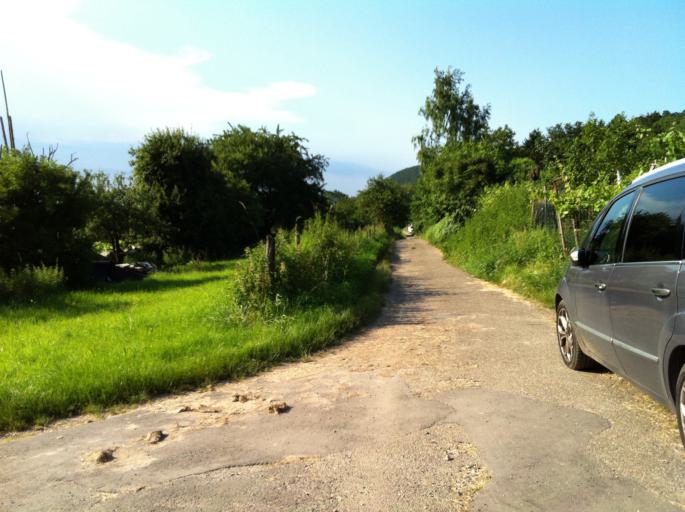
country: DE
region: Baden-Wuerttemberg
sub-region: Karlsruhe Region
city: Leimen
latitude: 49.3705
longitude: 8.6944
